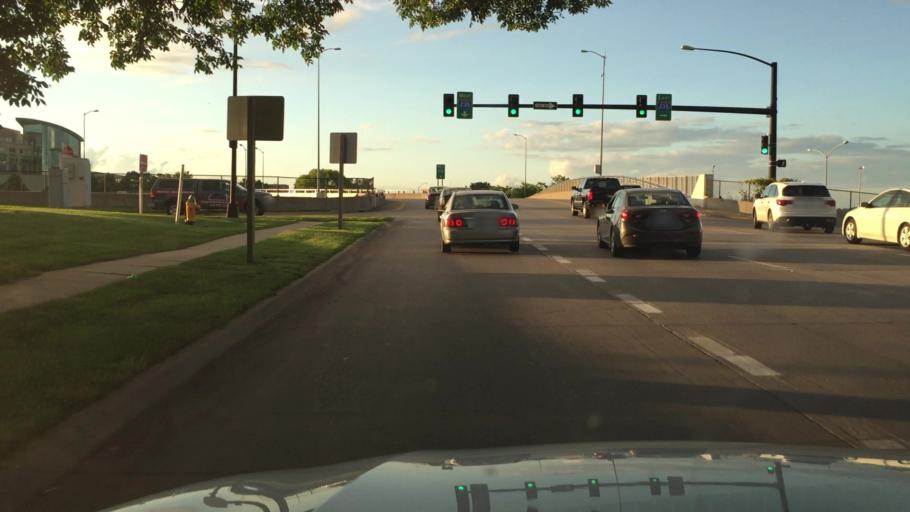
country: US
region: Iowa
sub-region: Polk County
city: Des Moines
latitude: 41.5948
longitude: -93.6200
